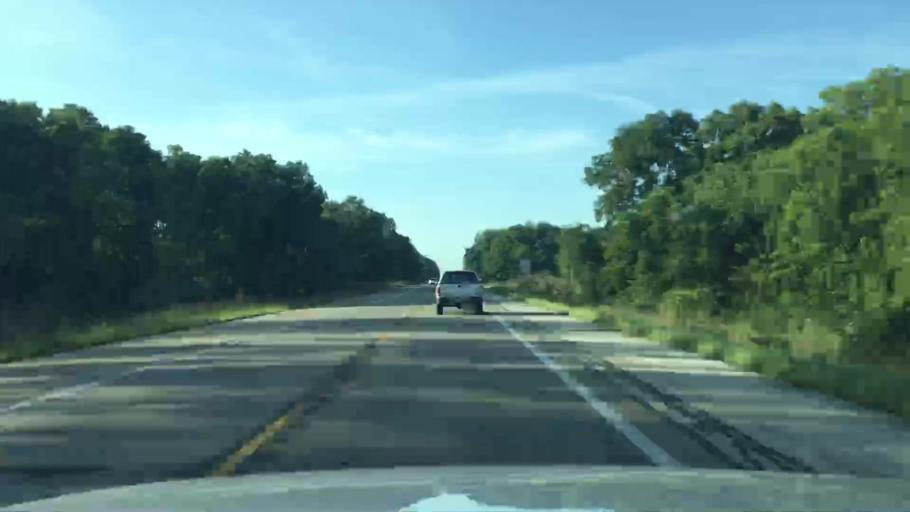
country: US
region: Michigan
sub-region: Jackson County
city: Vandercook Lake
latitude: 42.0931
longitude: -84.3638
